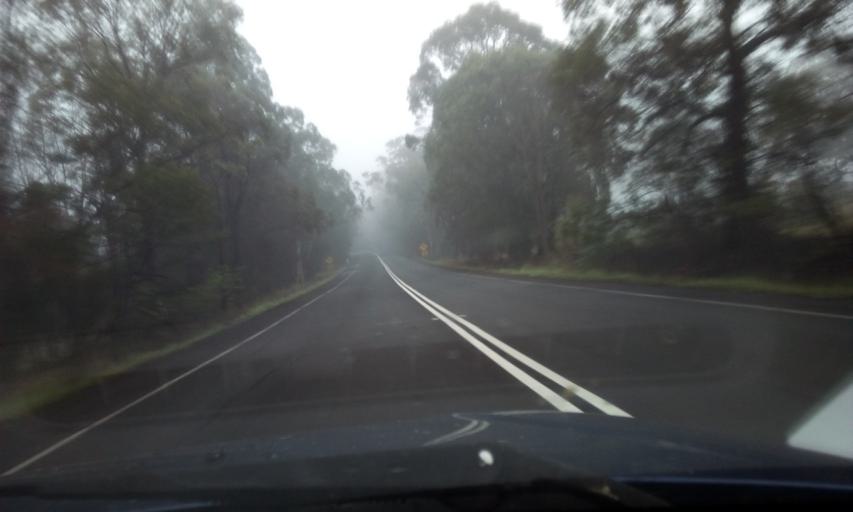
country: AU
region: New South Wales
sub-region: Wollondilly
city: Douglas Park
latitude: -34.2414
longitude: 150.7280
